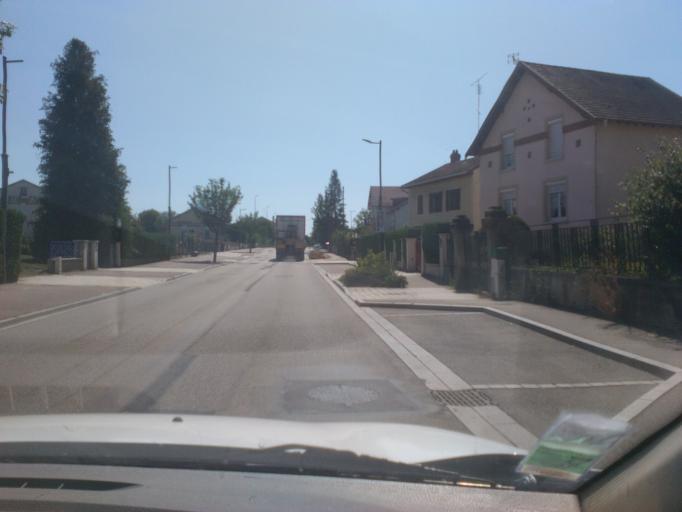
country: FR
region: Lorraine
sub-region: Departement des Vosges
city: Rambervillers
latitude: 48.3364
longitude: 6.6354
